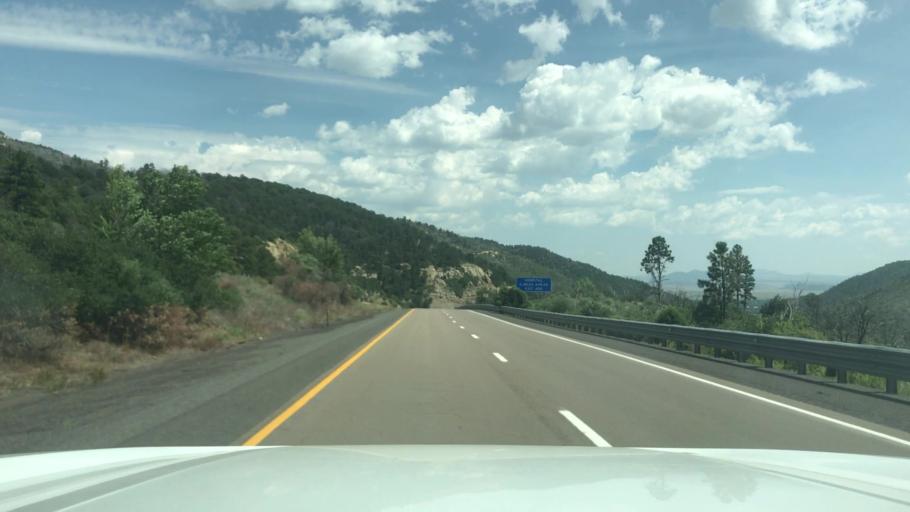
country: US
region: New Mexico
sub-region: Colfax County
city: Raton
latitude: 36.9341
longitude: -104.4630
